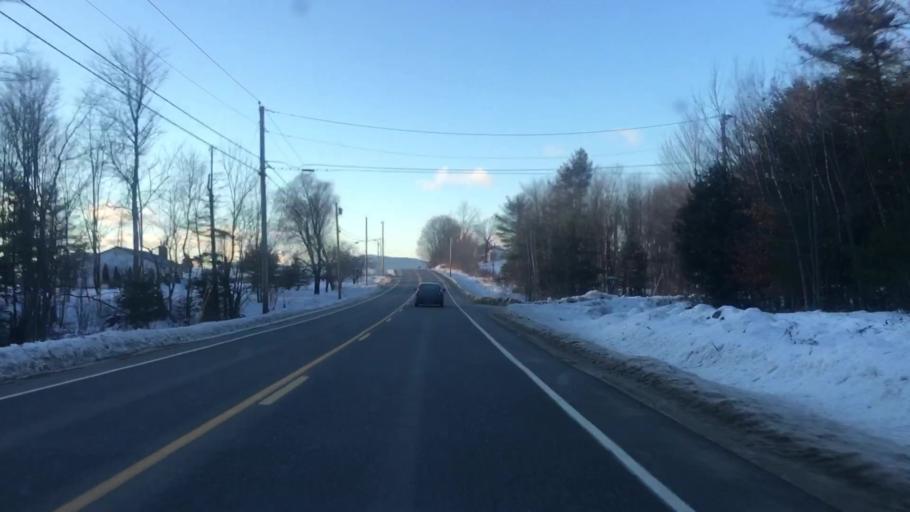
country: US
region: Maine
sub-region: Franklin County
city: Wilton
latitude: 44.5808
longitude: -70.1844
